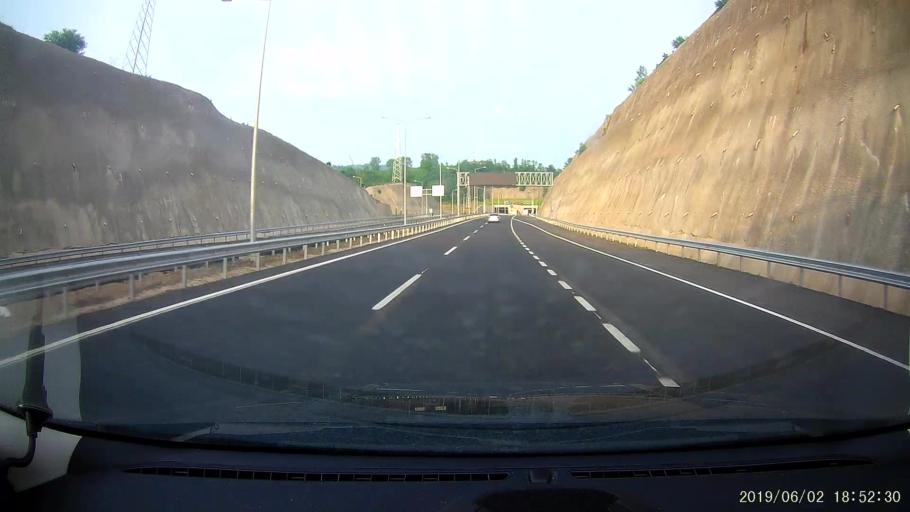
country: TR
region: Ordu
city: Ordu
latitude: 40.9886
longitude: 37.8130
